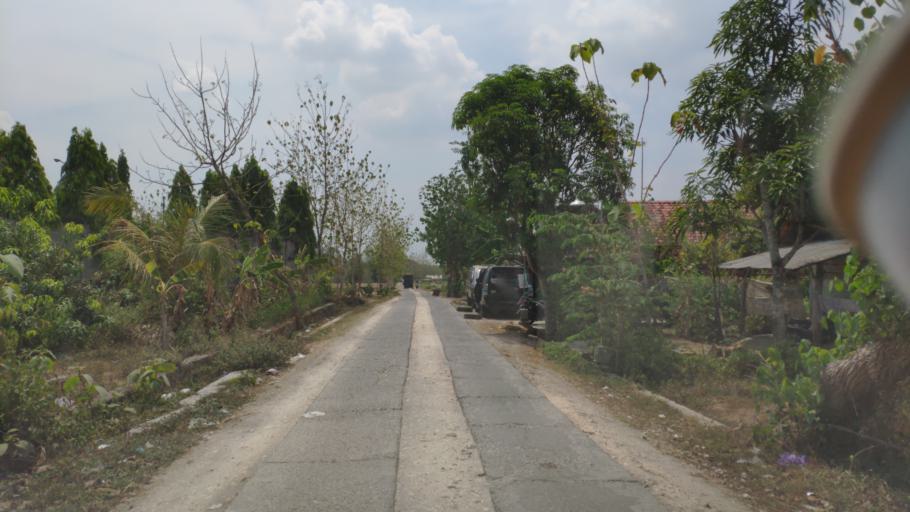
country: ID
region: Central Java
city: Berbak
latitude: -6.9968
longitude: 111.3188
